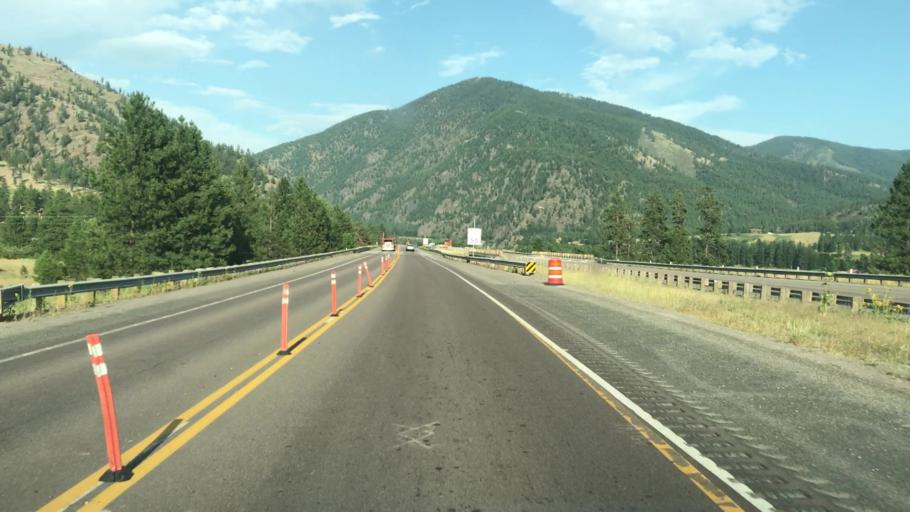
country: US
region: Montana
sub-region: Missoula County
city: Frenchtown
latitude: 47.0043
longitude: -114.5844
